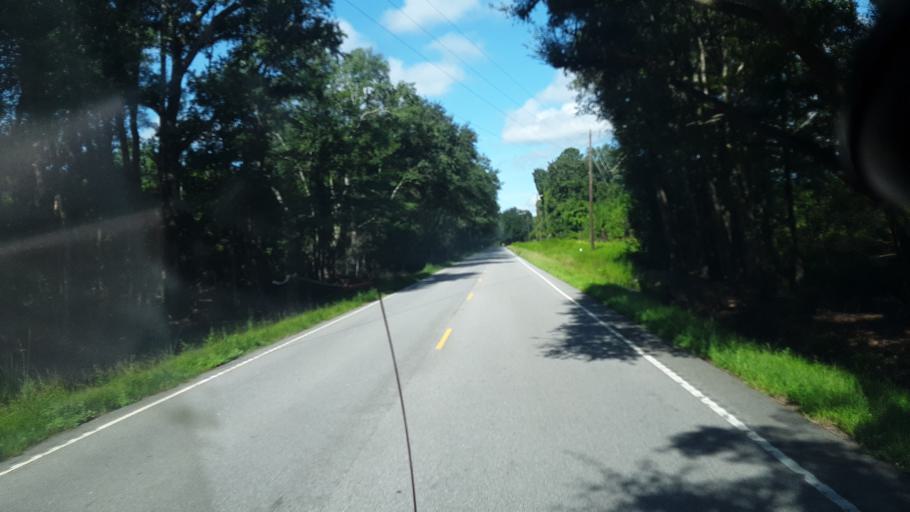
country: US
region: South Carolina
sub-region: Jasper County
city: Ridgeland
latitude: 32.5904
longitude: -80.9666
